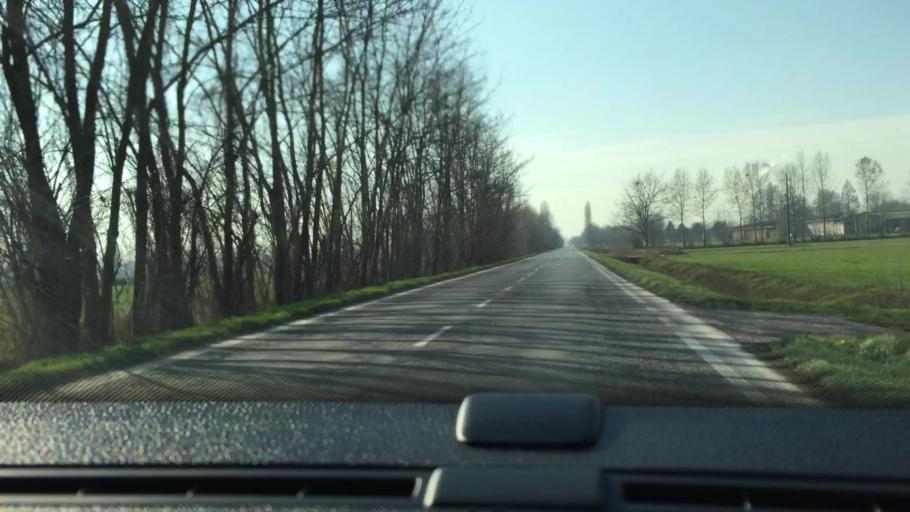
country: IT
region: Lombardy
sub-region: Provincia di Mantova
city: Goito
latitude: 45.2430
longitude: 10.6520
